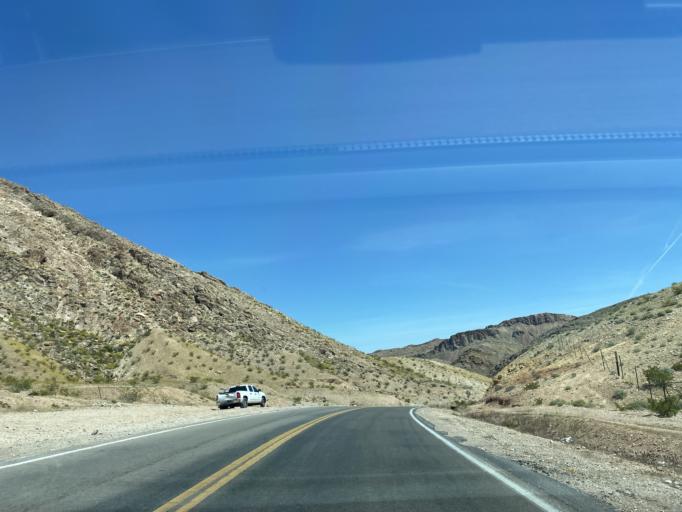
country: US
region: Nevada
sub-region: Clark County
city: Nellis Air Force Base
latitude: 36.2028
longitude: -114.9869
